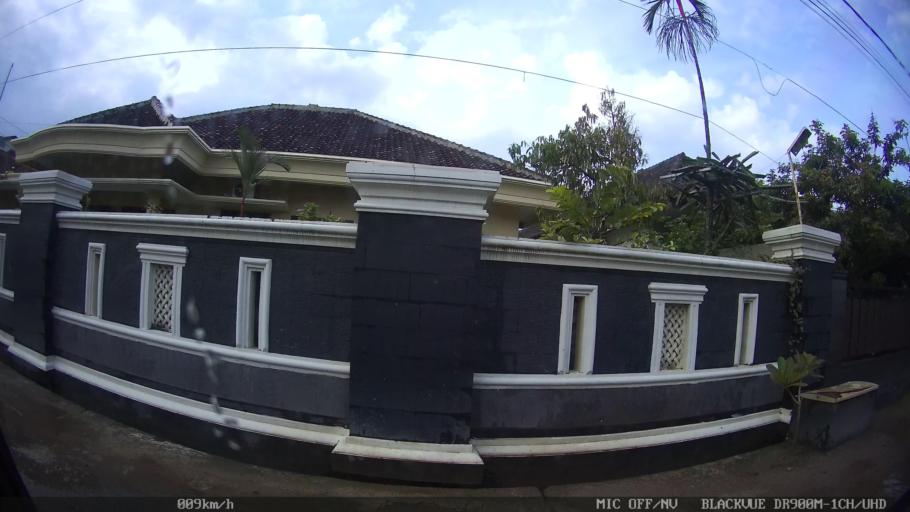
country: ID
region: Lampung
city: Kedaton
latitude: -5.3889
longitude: 105.2963
